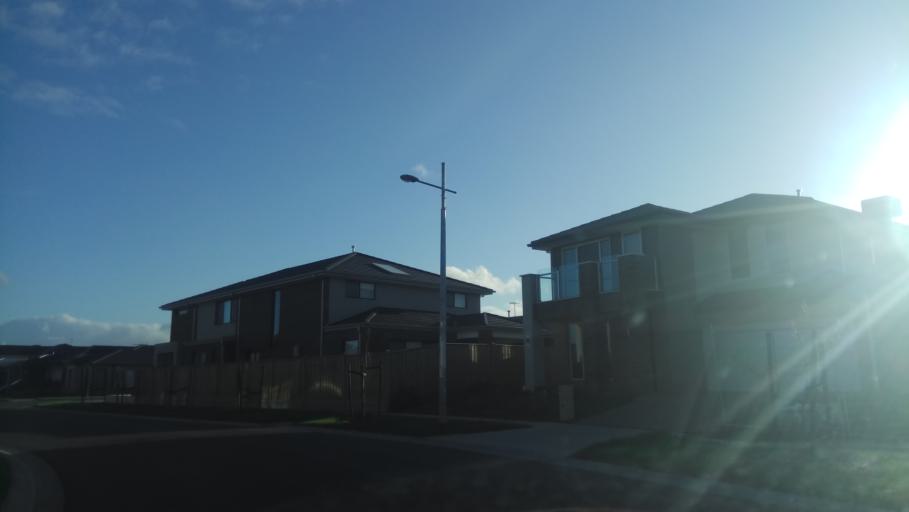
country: AU
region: Victoria
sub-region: Hobsons Bay
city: Altona Meadows
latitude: -37.9122
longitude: 144.7834
